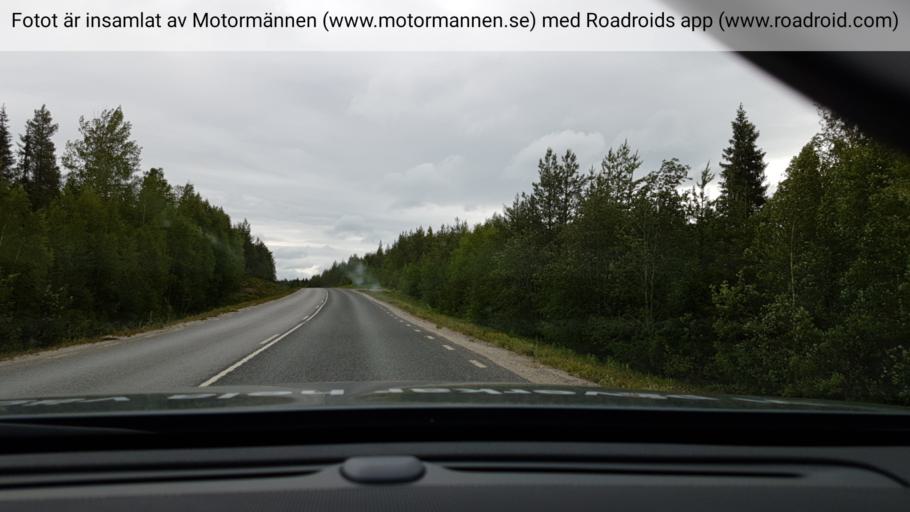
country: SE
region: Vaesterbotten
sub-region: Lycksele Kommun
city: Lycksele
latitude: 64.5123
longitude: 18.3612
